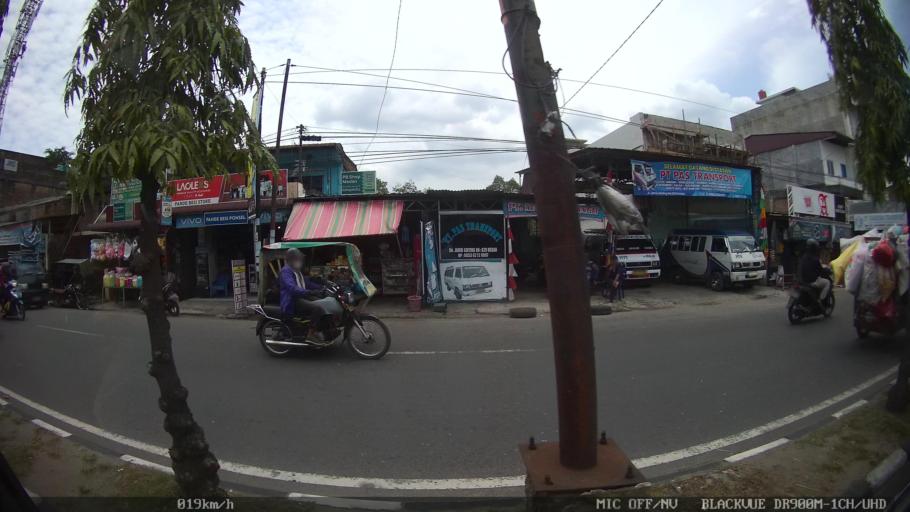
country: ID
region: North Sumatra
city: Medan
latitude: 3.5496
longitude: 98.6598
